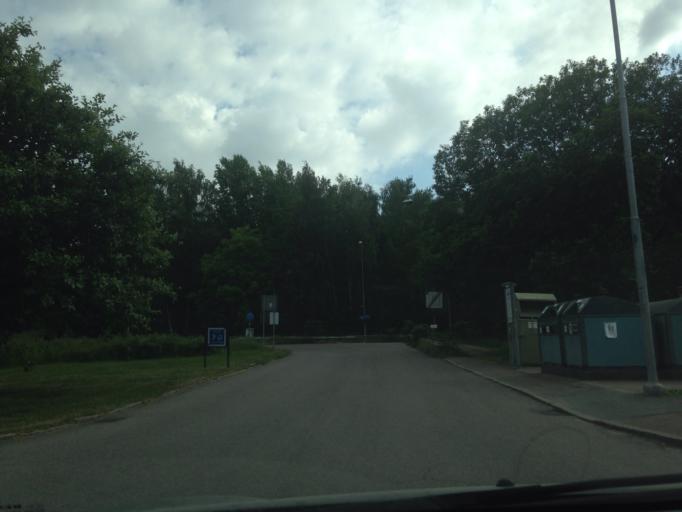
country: SE
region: Vaestra Goetaland
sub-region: Goteborg
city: Majorna
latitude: 57.7467
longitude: 11.9184
